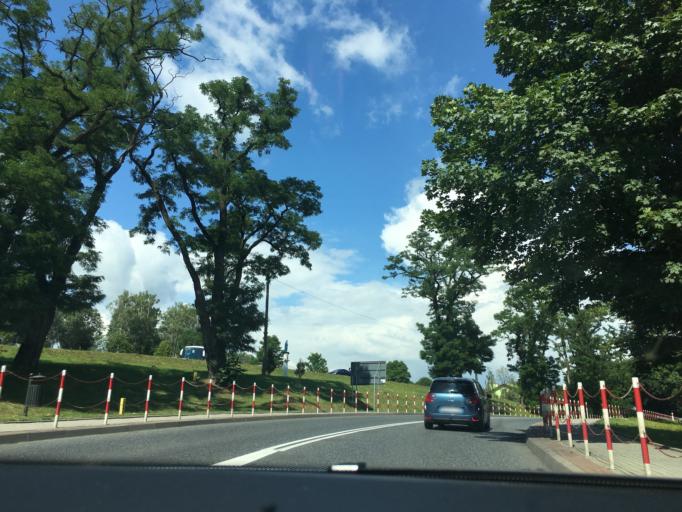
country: PL
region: Subcarpathian Voivodeship
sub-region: Powiat krosnienski
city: Dukla
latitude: 49.5585
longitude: 21.6833
